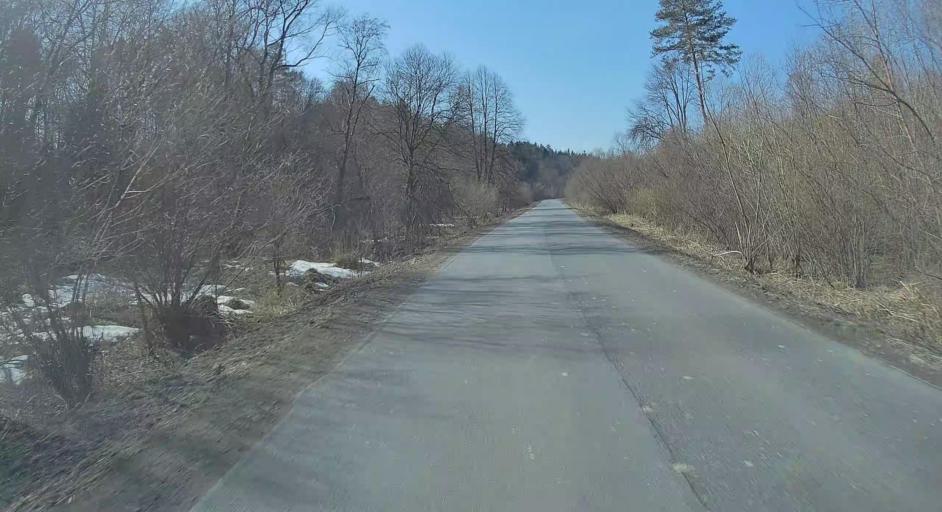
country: PL
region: Subcarpathian Voivodeship
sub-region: Powiat przemyski
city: Bircza
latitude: 49.6973
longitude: 22.3599
